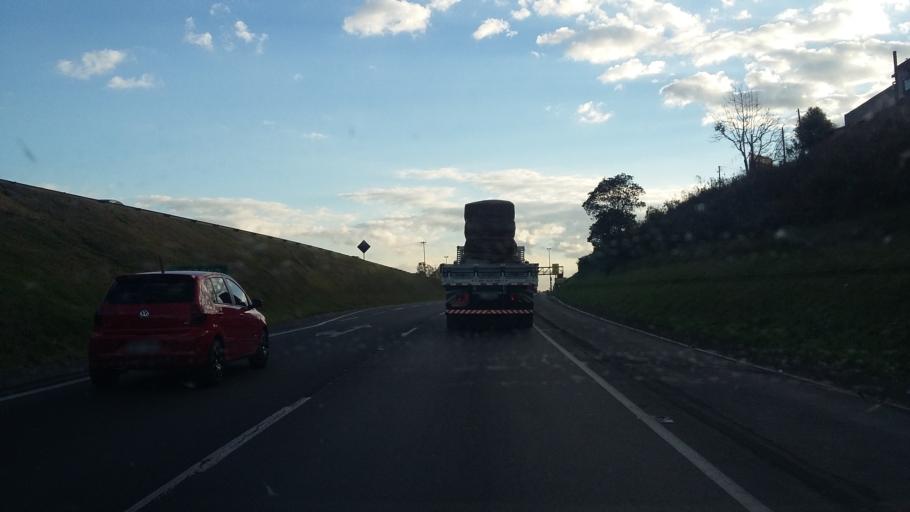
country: BR
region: Parana
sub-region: Curitiba
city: Curitiba
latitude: -25.4324
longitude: -49.4021
